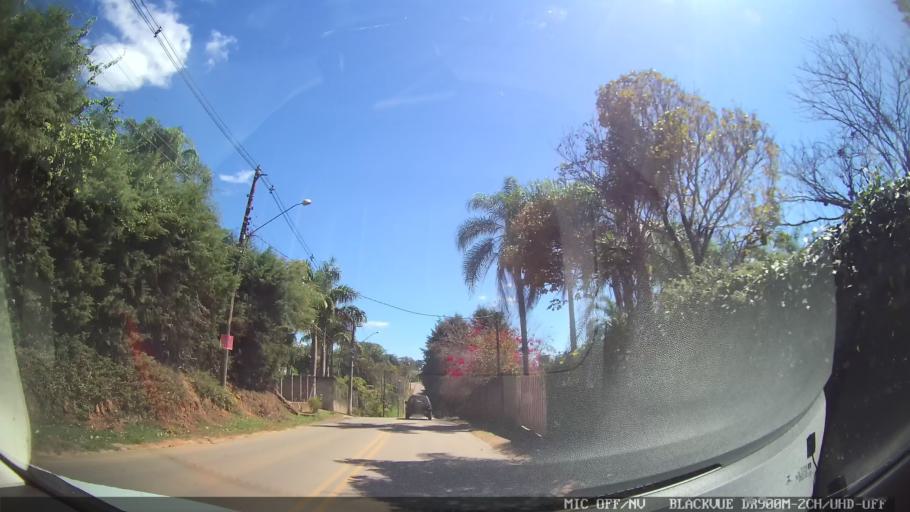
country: BR
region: Sao Paulo
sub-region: Campo Limpo Paulista
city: Campo Limpo Paulista
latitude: -23.1788
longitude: -46.7589
